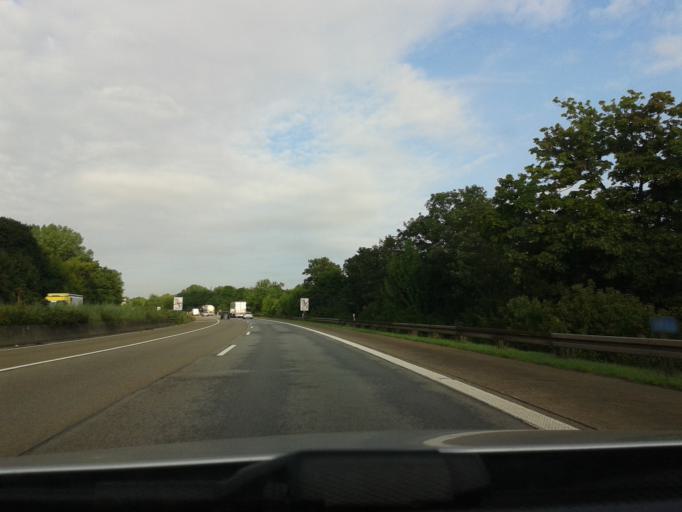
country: DE
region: North Rhine-Westphalia
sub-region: Regierungsbezirk Dusseldorf
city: Hochfeld
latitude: 51.4387
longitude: 6.7268
